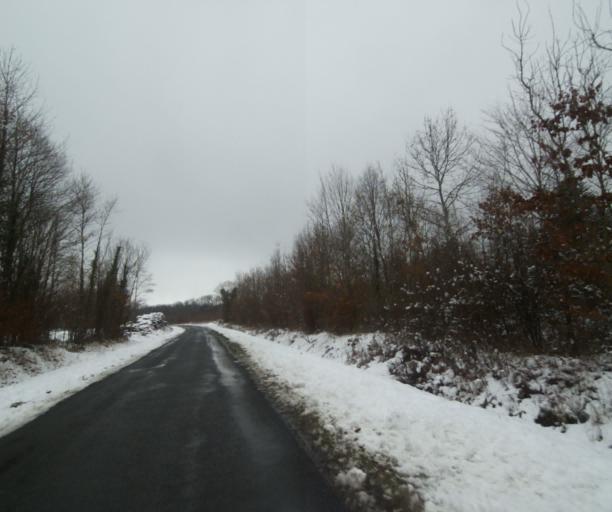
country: FR
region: Champagne-Ardenne
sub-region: Departement de la Haute-Marne
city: Laneuville-a-Remy
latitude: 48.4703
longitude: 4.8738
